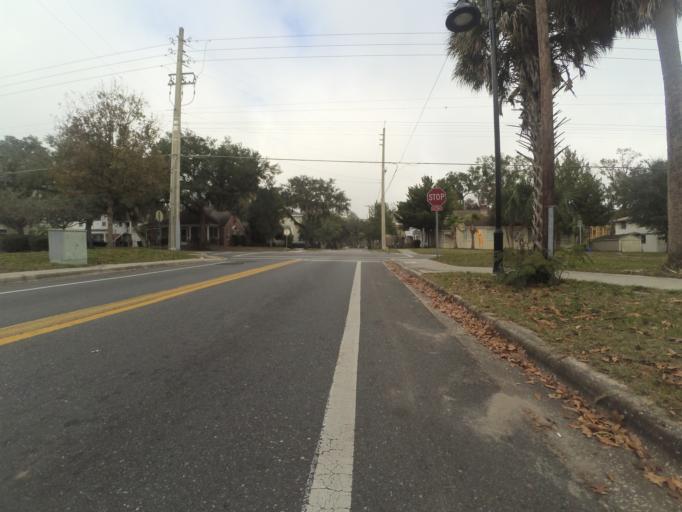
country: US
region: Florida
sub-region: Alachua County
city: Gainesville
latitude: 29.6480
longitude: -82.3370
